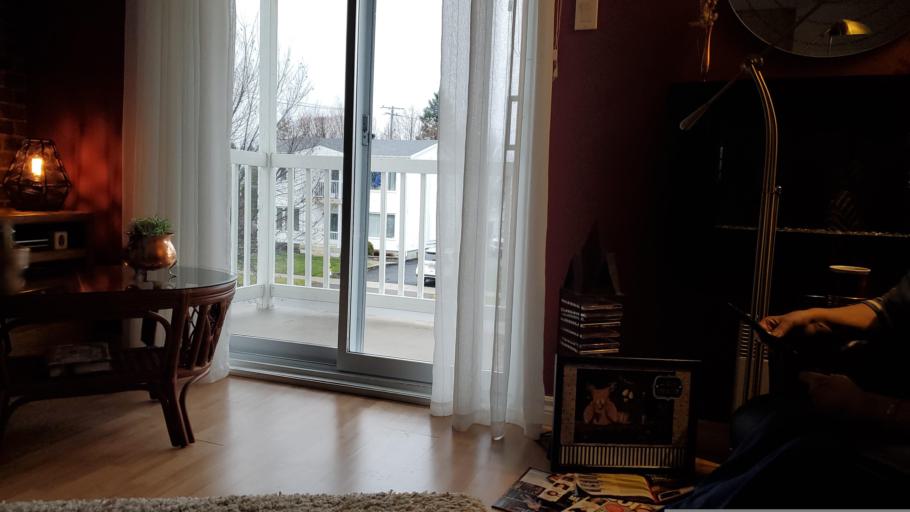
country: CA
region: Quebec
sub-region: Saguenay/Lac-Saint-Jean
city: Saguenay
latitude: 48.4156
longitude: -71.0704
